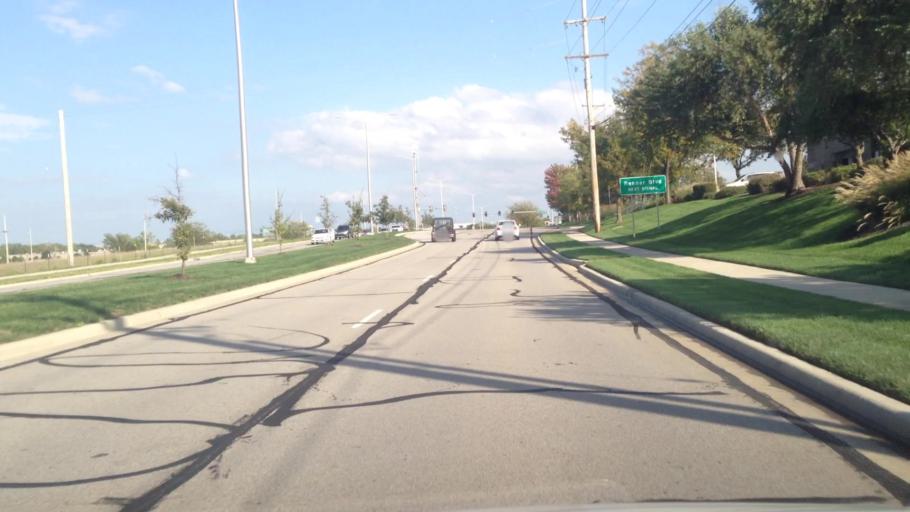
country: US
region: Kansas
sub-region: Johnson County
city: Lenexa
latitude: 38.9273
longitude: -94.7822
